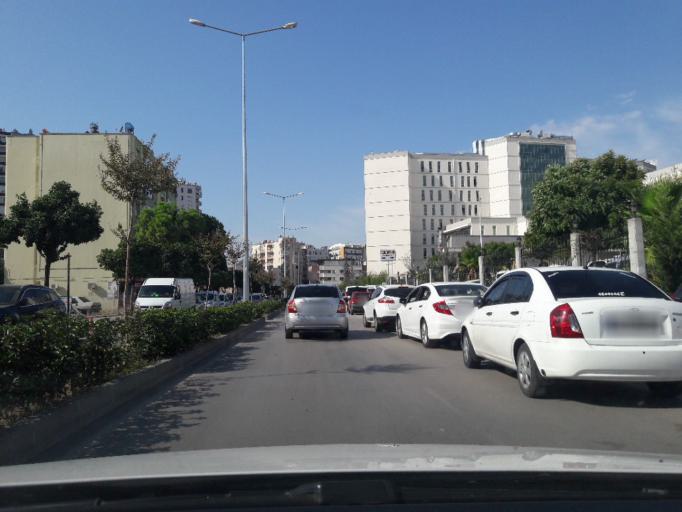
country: TR
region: Adana
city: Adana
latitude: 37.0188
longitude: 35.3203
